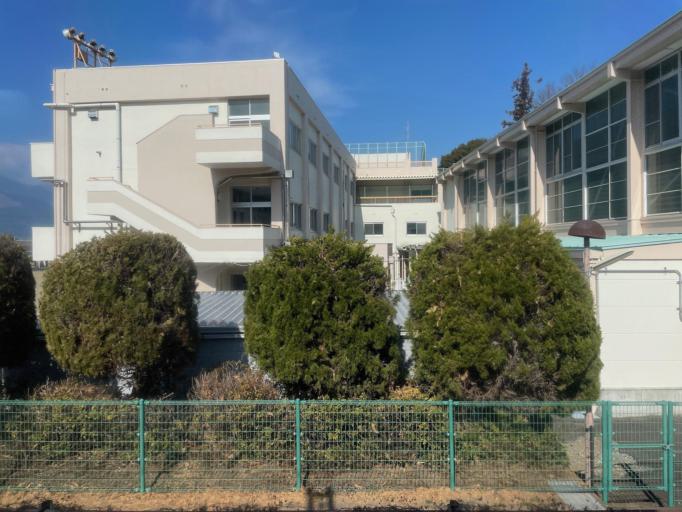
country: JP
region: Yamanashi
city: Ryuo
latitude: 35.5642
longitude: 138.5118
